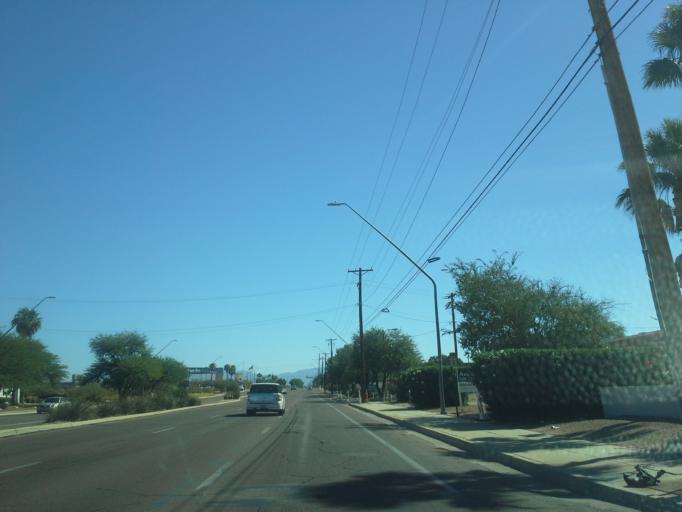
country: US
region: Arizona
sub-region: Pima County
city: Summit
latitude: 32.1341
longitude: -110.9300
